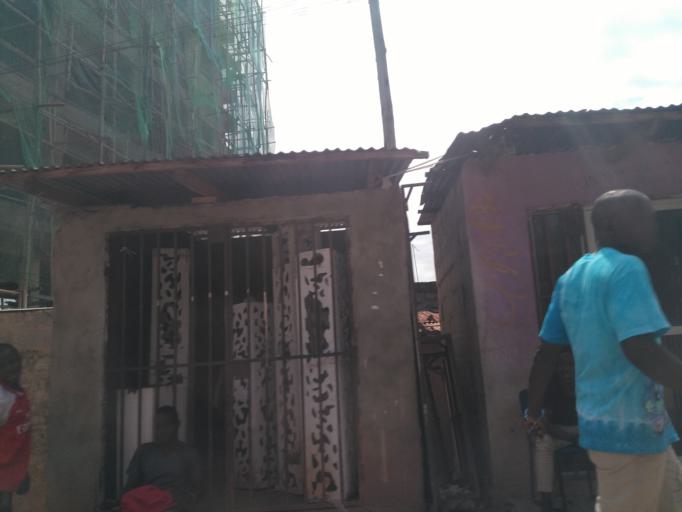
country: TZ
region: Dar es Salaam
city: Magomeni
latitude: -6.7784
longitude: 39.2720
